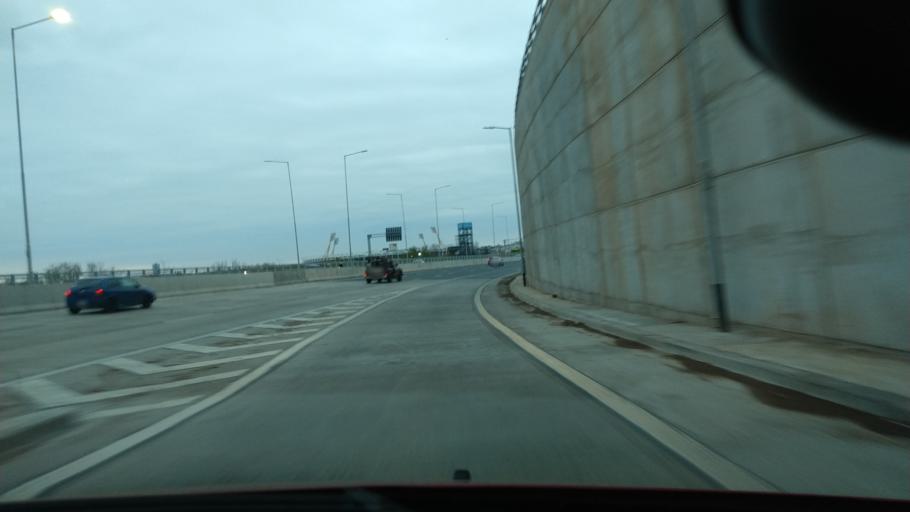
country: AR
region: Cordoba
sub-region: Departamento de Capital
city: Cordoba
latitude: -31.3608
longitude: -64.2419
